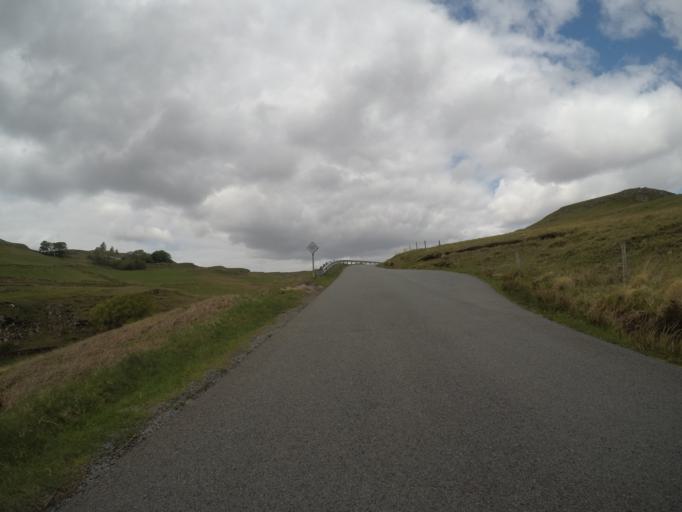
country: GB
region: Scotland
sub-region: Highland
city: Isle of Skye
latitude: 57.3625
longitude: -6.3976
